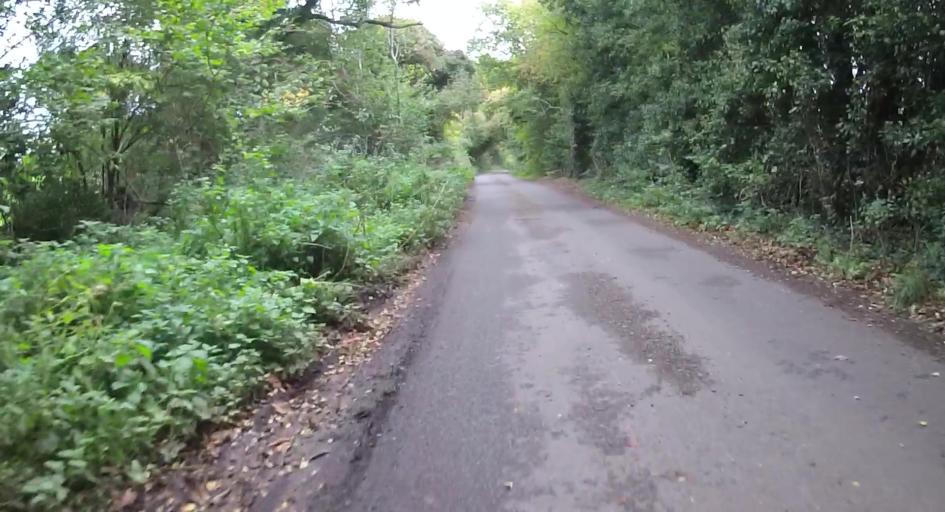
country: GB
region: England
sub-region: Hampshire
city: Four Marks
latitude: 51.0996
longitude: -1.0528
